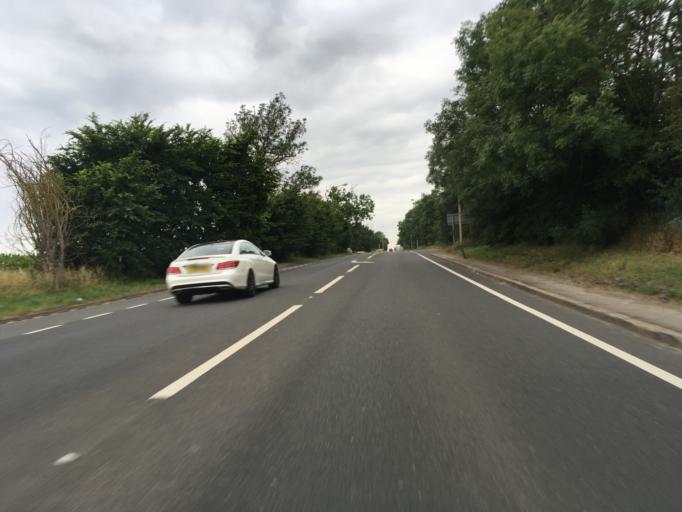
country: GB
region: England
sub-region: Central Bedfordshire
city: Hockliffe
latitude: 51.9167
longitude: -0.5650
